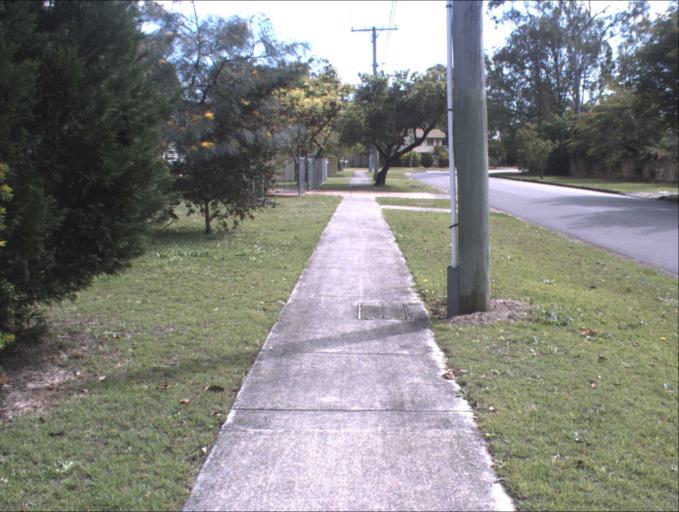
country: AU
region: Queensland
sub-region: Logan
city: Waterford West
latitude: -27.6796
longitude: 153.1102
